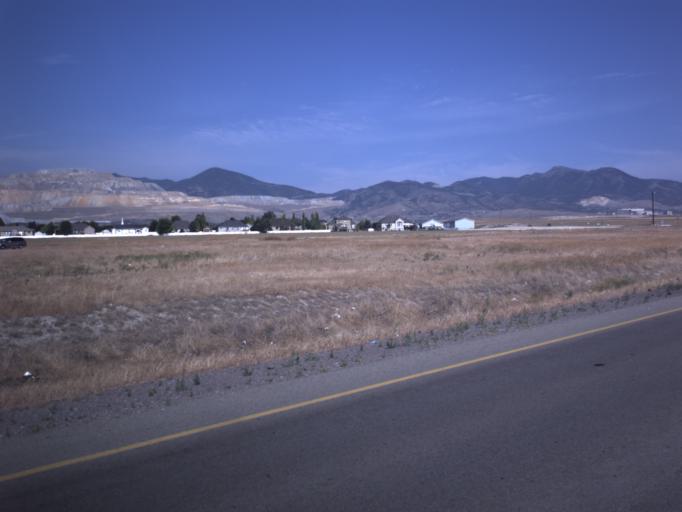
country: US
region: Utah
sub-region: Salt Lake County
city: Herriman
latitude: 40.5415
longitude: -112.0190
